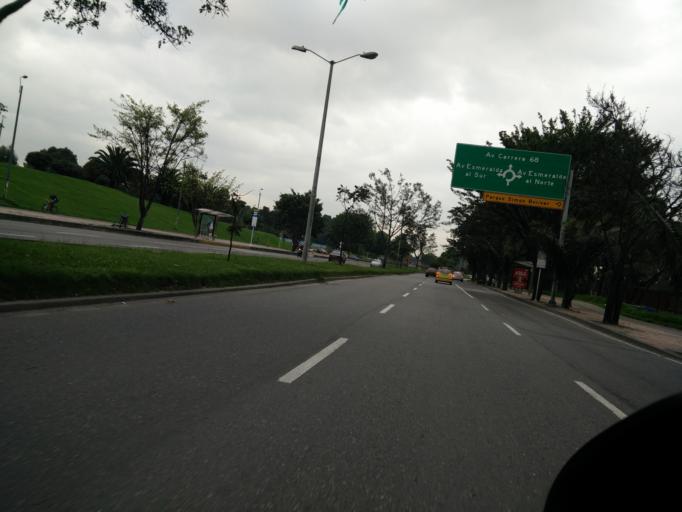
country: CO
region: Bogota D.C.
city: Bogota
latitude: 4.6579
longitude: -74.0875
